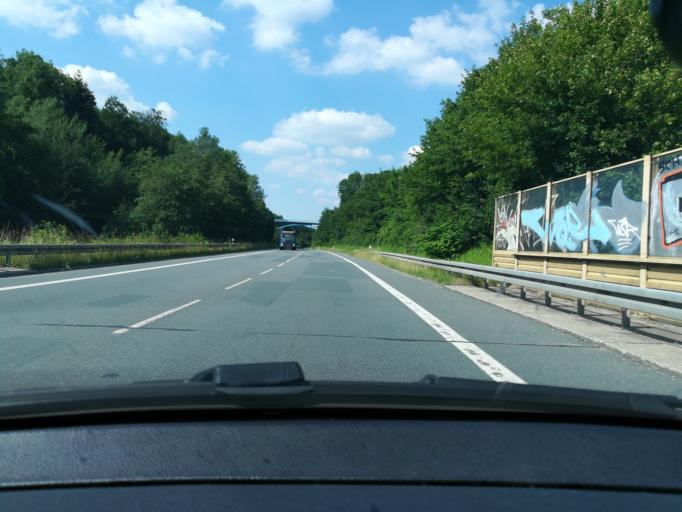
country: DE
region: North Rhine-Westphalia
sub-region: Regierungsbezirk Detmold
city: Oerlinghausen
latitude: 51.9638
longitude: 8.6573
